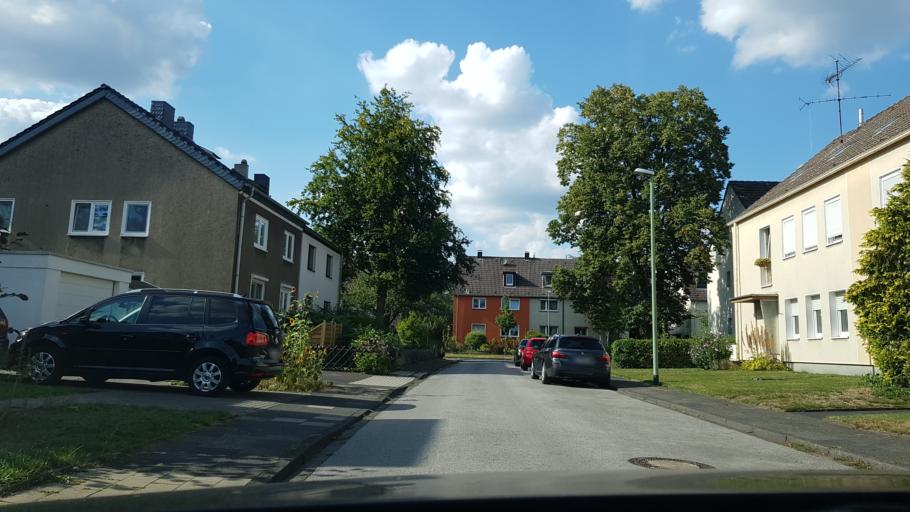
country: DE
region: North Rhine-Westphalia
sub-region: Regierungsbezirk Dusseldorf
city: Hochfeld
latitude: 51.3934
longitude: 6.7884
